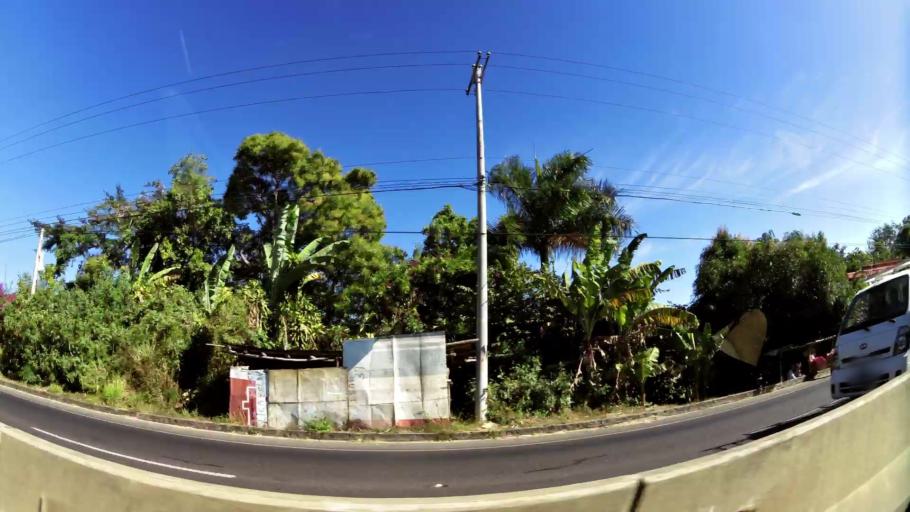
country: SV
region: Santa Ana
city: Santa Ana
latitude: 13.9447
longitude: -89.5536
